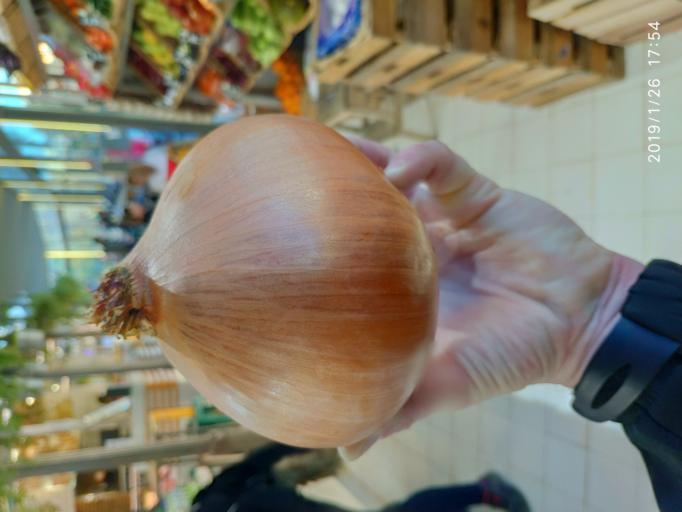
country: ES
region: Andalusia
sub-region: Province of Cordoba
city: Cordoba
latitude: 37.8838
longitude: -4.7854
